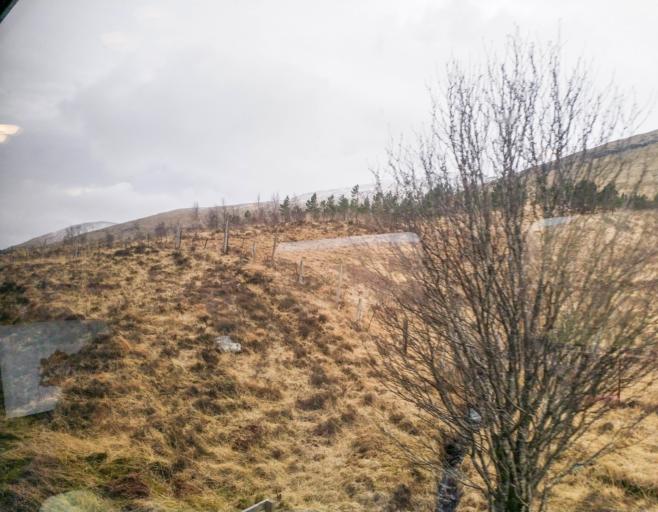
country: GB
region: Scotland
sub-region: Highland
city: Spean Bridge
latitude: 56.5653
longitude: -4.7035
